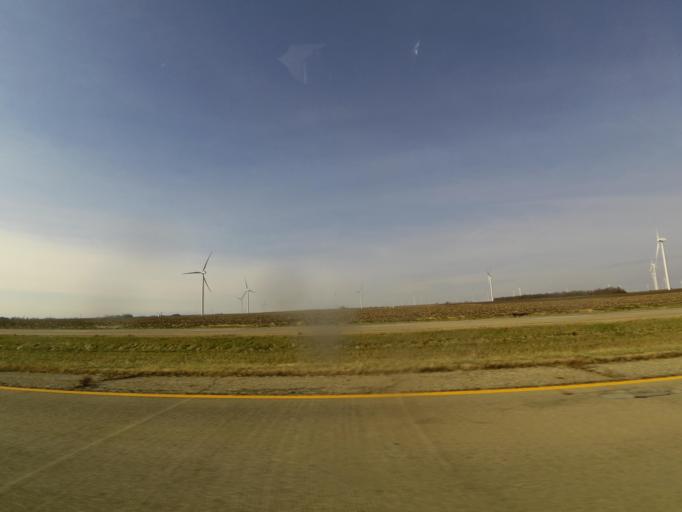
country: US
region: Illinois
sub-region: Macon County
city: Forsyth
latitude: 39.9768
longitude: -88.9560
